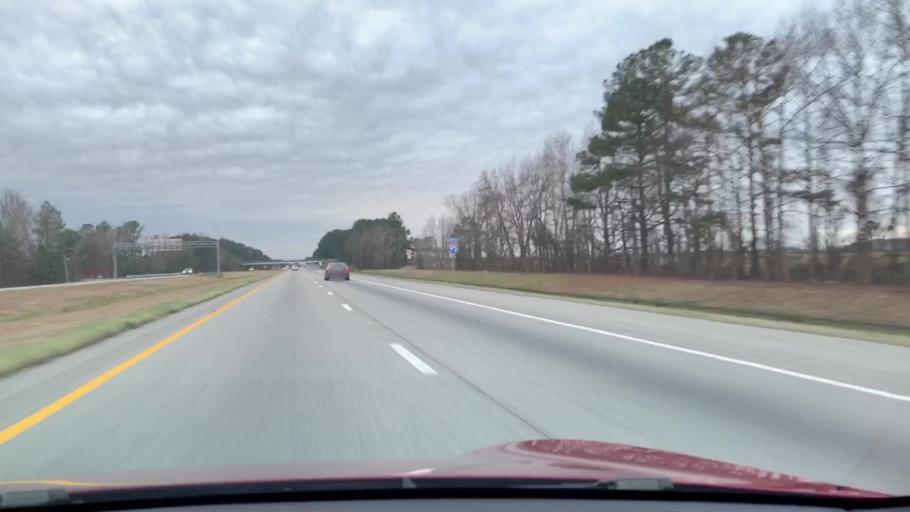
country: US
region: North Carolina
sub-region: Robeson County
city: Fairmont
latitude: 34.5726
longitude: -79.1598
